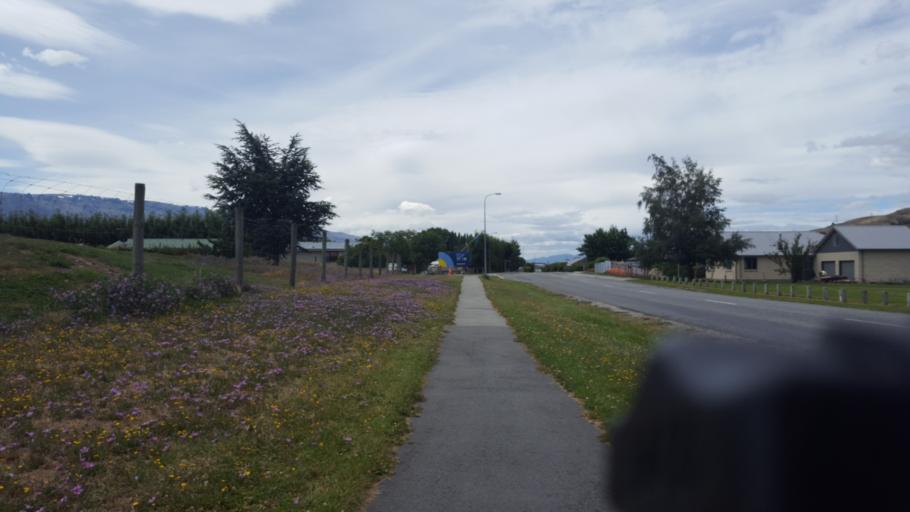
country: NZ
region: Otago
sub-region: Queenstown-Lakes District
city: Wanaka
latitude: -45.0411
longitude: 169.2144
